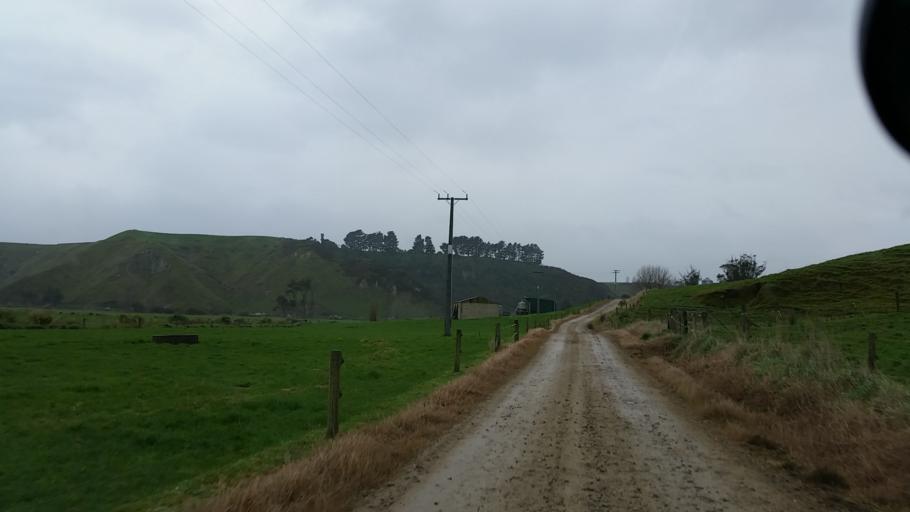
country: NZ
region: Taranaki
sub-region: South Taranaki District
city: Patea
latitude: -39.7576
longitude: 174.7092
